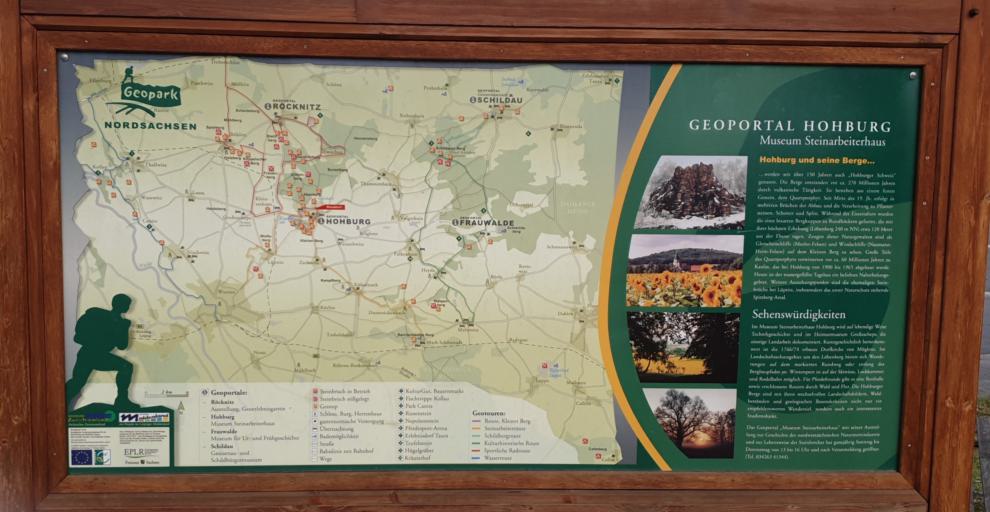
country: DE
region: Saxony
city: Hohburg
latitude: 51.4114
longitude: 12.7981
